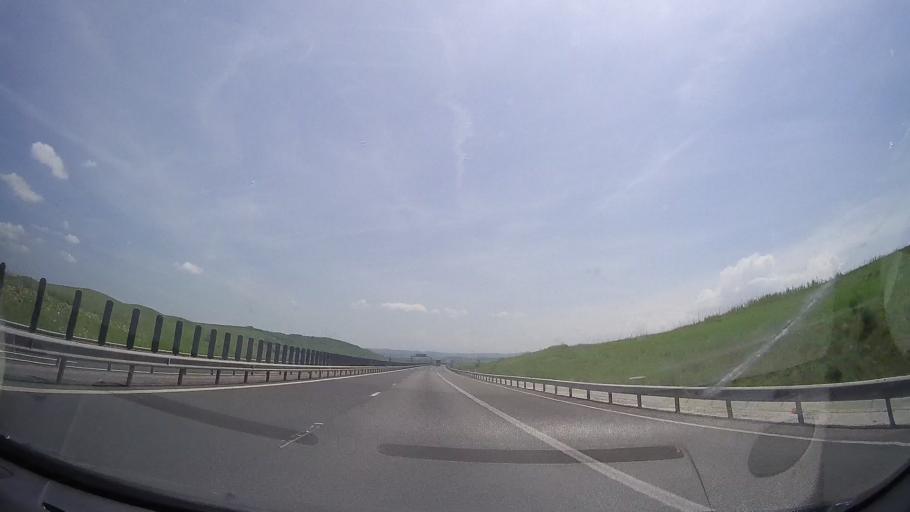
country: RO
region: Alba
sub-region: Comuna Garbova
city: Garbova
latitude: 45.9170
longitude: 23.7265
